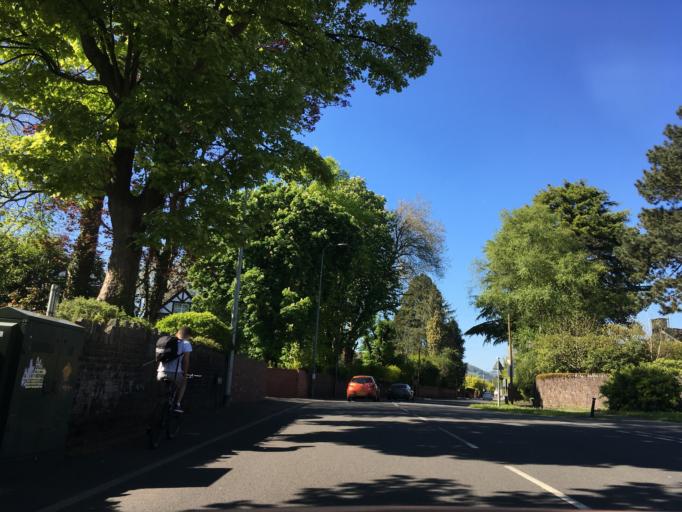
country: GB
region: Wales
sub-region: Cardiff
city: Radyr
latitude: 51.5091
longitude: -3.2279
